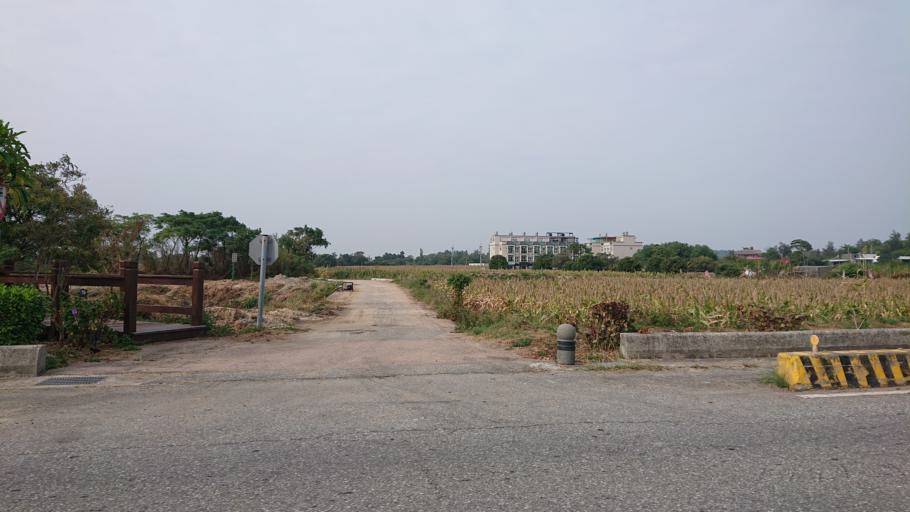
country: TW
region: Fukien
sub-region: Kinmen
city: Jincheng
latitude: 24.4782
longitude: 118.4229
